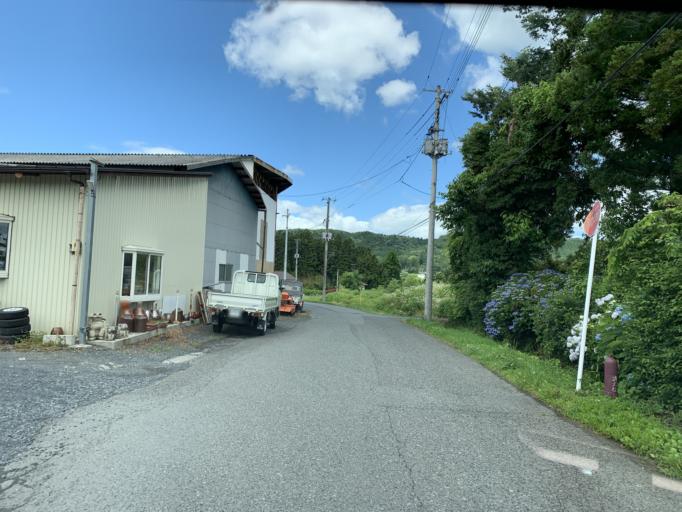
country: JP
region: Iwate
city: Ichinoseki
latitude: 38.9350
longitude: 141.0794
